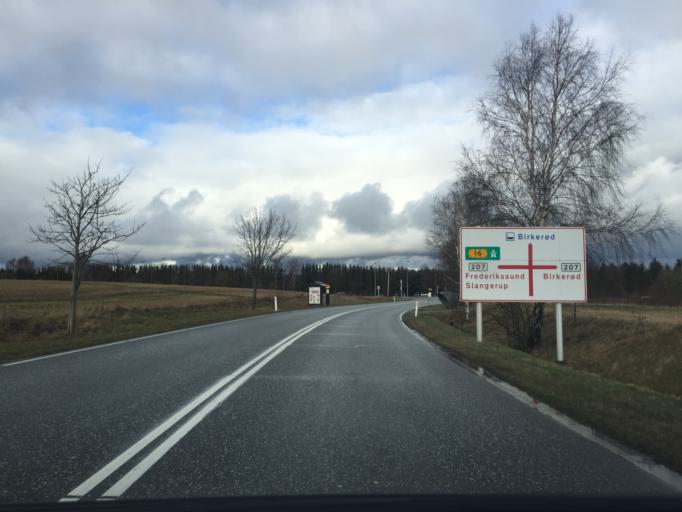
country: DK
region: Capital Region
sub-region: Fureso Kommune
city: Stavnsholt
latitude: 55.8224
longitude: 12.3999
